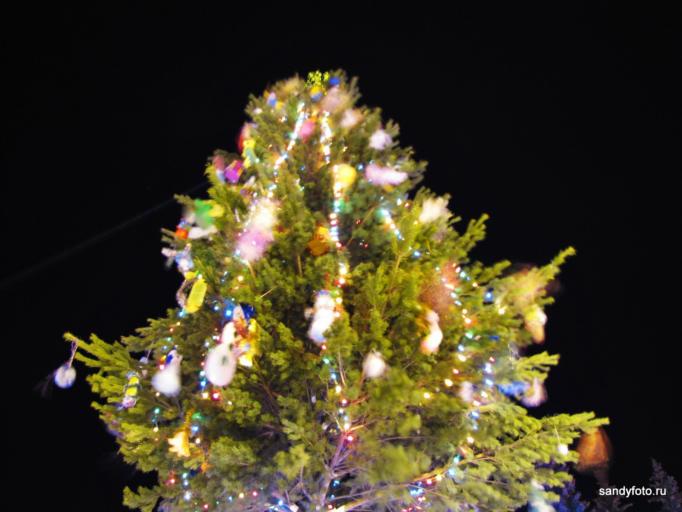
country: RU
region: Chelyabinsk
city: Troitsk
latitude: 54.0830
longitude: 61.5593
